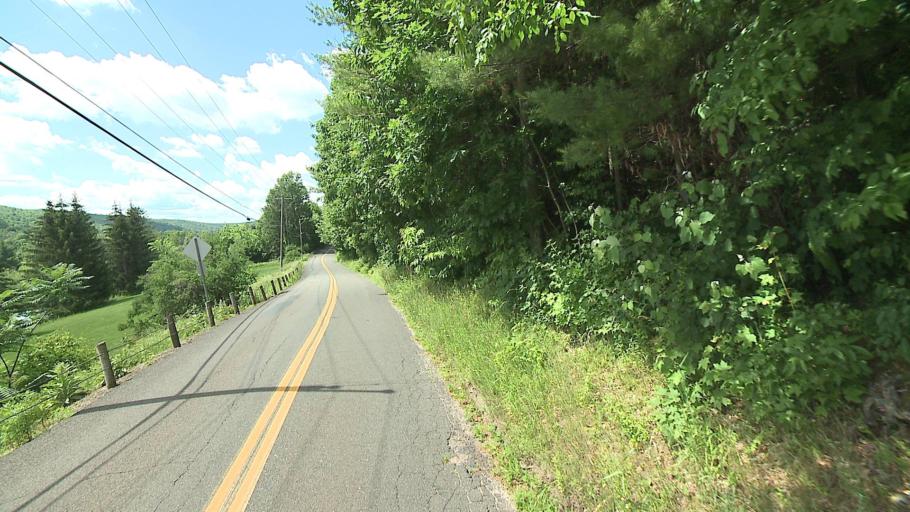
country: US
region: Connecticut
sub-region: Litchfield County
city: Litchfield
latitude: 41.8392
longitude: -73.3174
